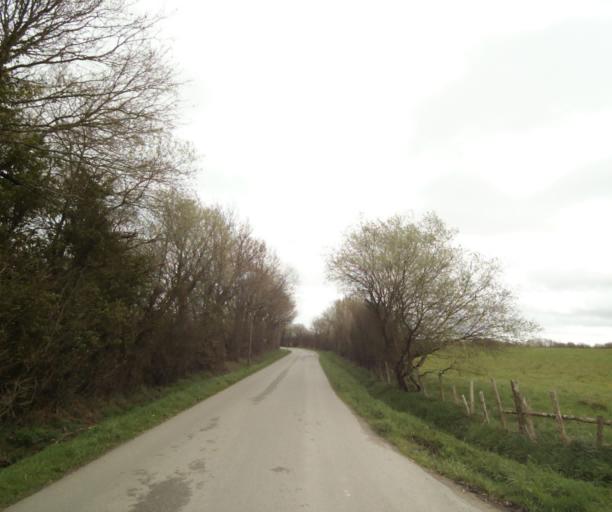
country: FR
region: Pays de la Loire
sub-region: Departement de la Loire-Atlantique
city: Bouvron
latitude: 47.4343
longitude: -1.8918
